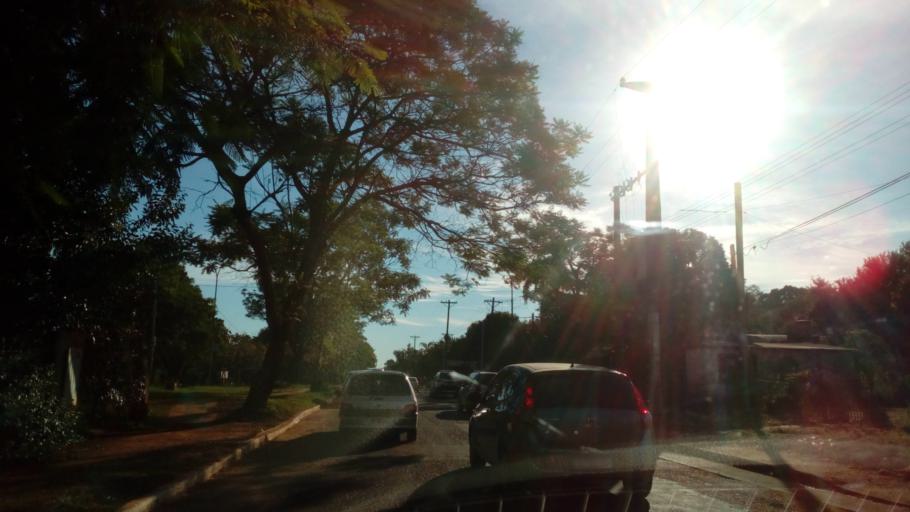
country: AR
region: Misiones
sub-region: Departamento de Capital
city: Posadas
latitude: -27.4304
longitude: -55.8825
